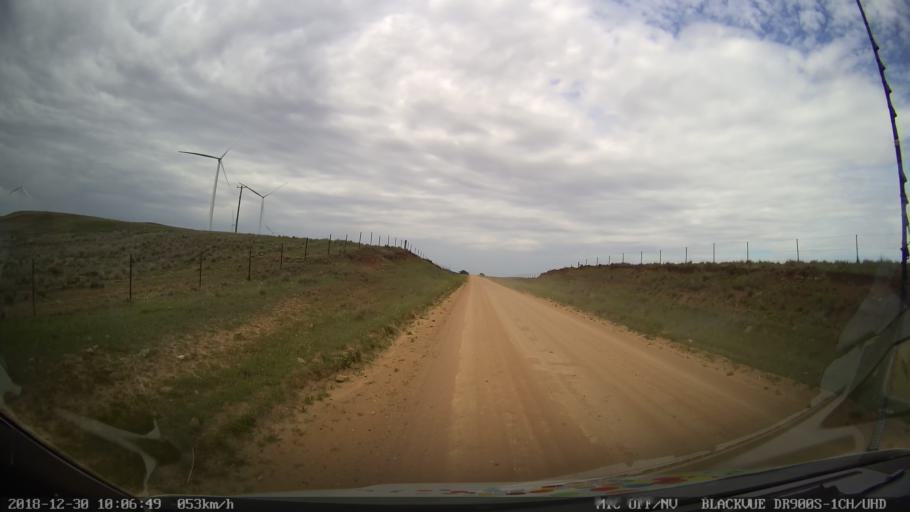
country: AU
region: New South Wales
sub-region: Cooma-Monaro
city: Cooma
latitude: -36.5352
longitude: 149.1271
